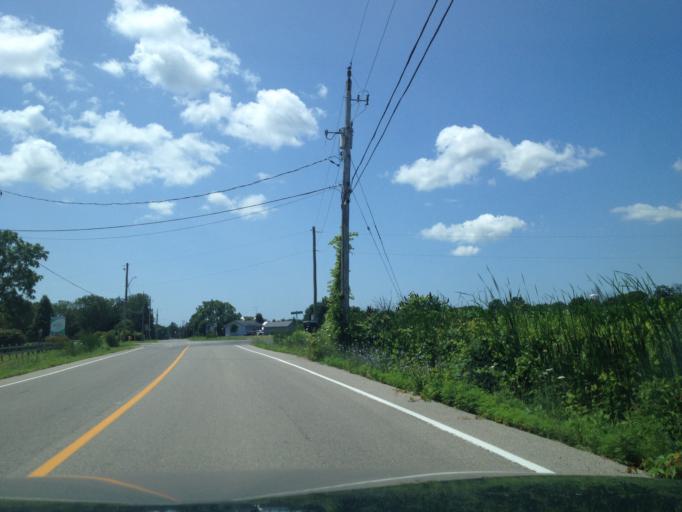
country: CA
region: Ontario
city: Norfolk County
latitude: 42.6354
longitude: -80.4409
